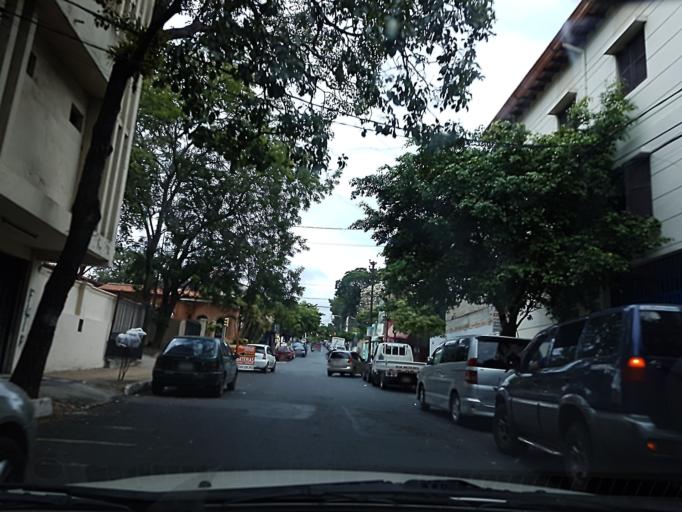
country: PY
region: Asuncion
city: Asuncion
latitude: -25.2891
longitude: -57.6306
